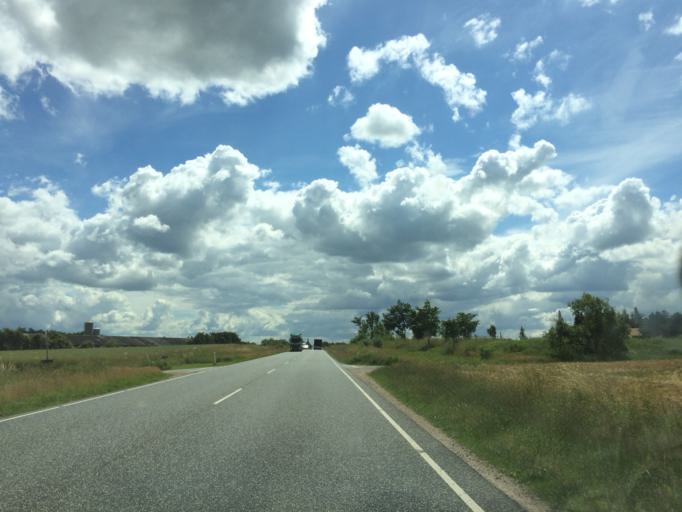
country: DK
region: North Denmark
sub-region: Vesthimmerland Kommune
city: Alestrup
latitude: 56.6011
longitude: 9.5012
